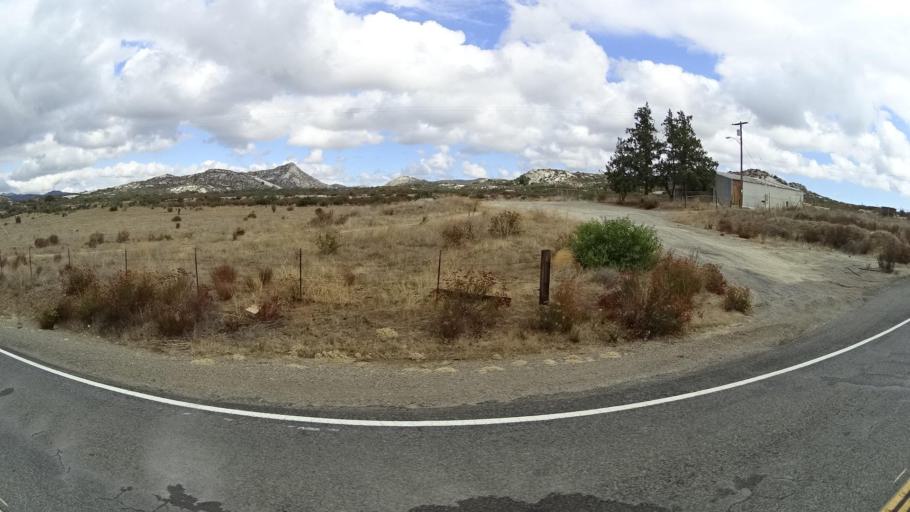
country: US
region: California
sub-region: San Diego County
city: Campo
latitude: 32.6301
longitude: -116.4401
